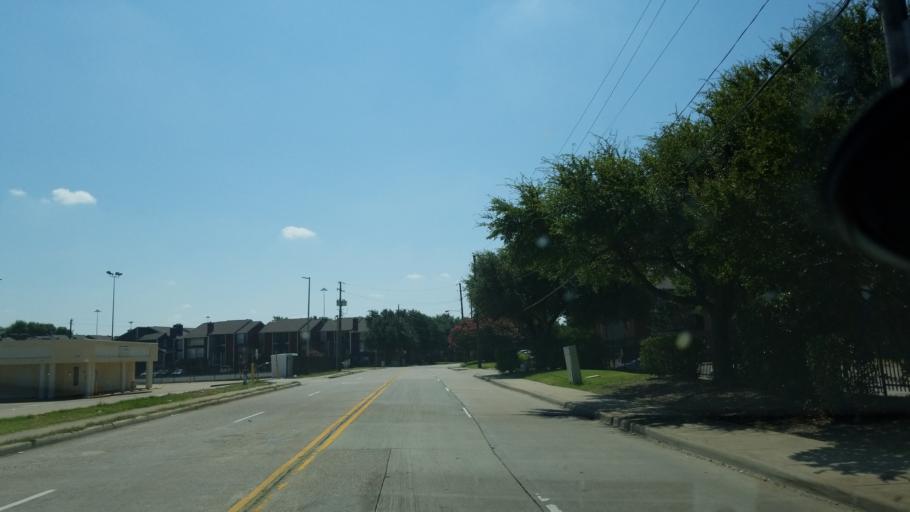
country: US
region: Texas
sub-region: Dallas County
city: Duncanville
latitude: 32.6545
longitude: -96.8850
